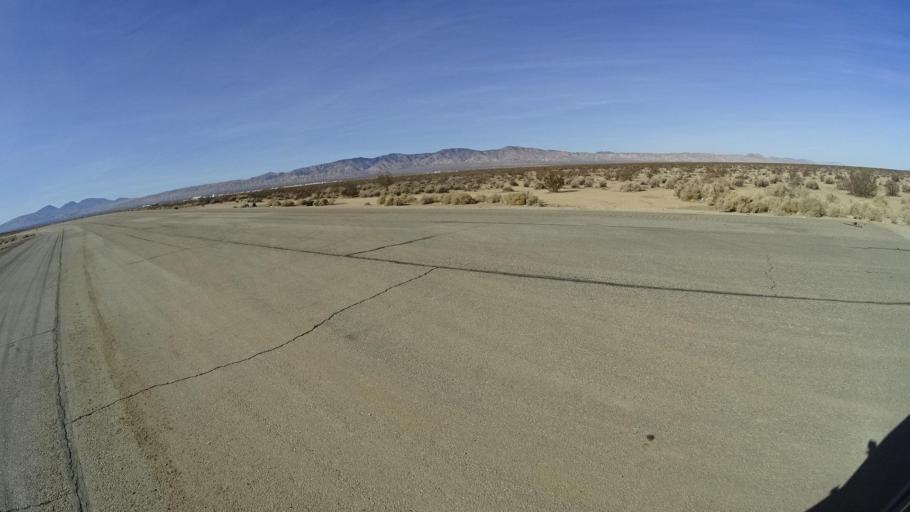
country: US
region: California
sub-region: Kern County
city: Mojave
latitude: 35.0411
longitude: -118.0980
